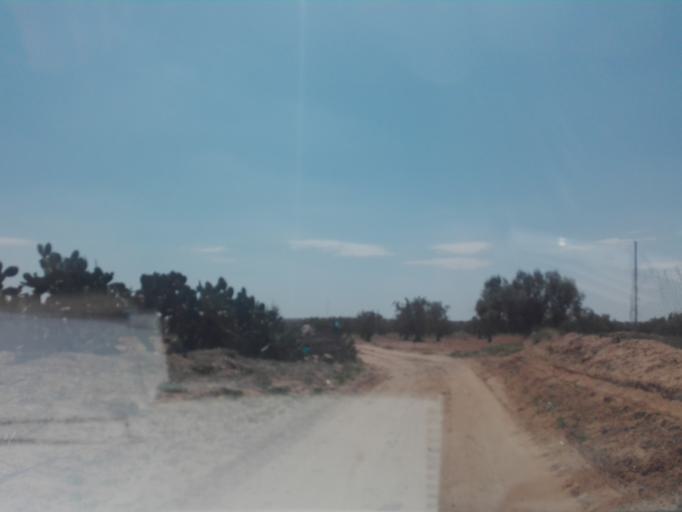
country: TN
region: Safaqis
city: Bi'r `Ali Bin Khalifah
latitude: 34.6111
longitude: 10.3525
